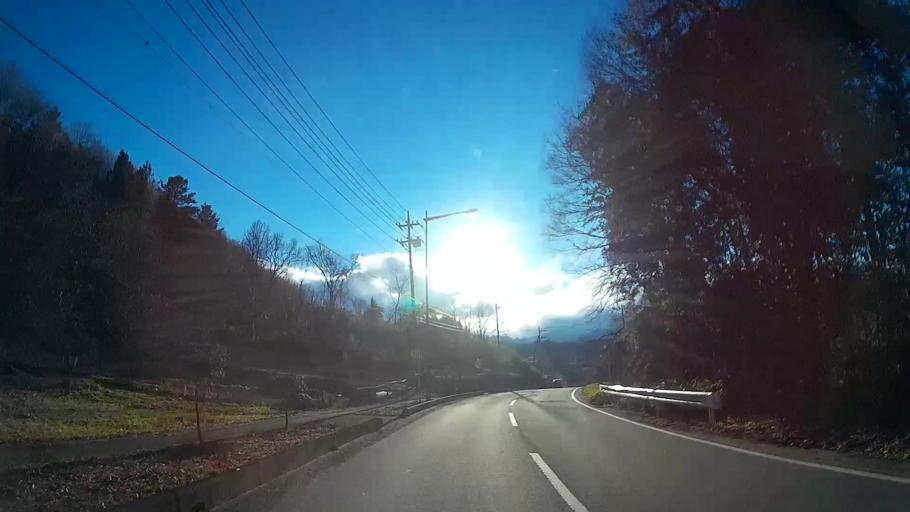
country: JP
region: Saitama
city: Chichibu
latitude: 36.0459
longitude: 139.0489
